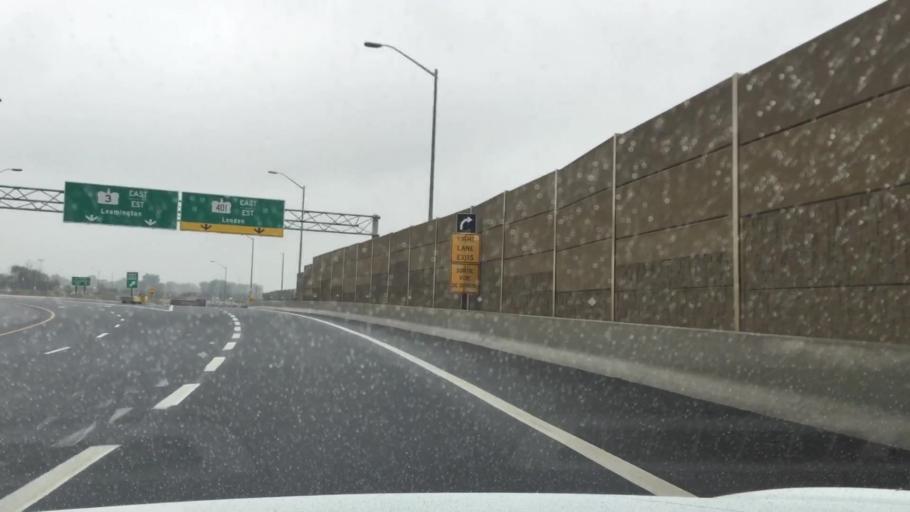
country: CA
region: Ontario
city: Windsor
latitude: 42.2648
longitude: -83.0455
